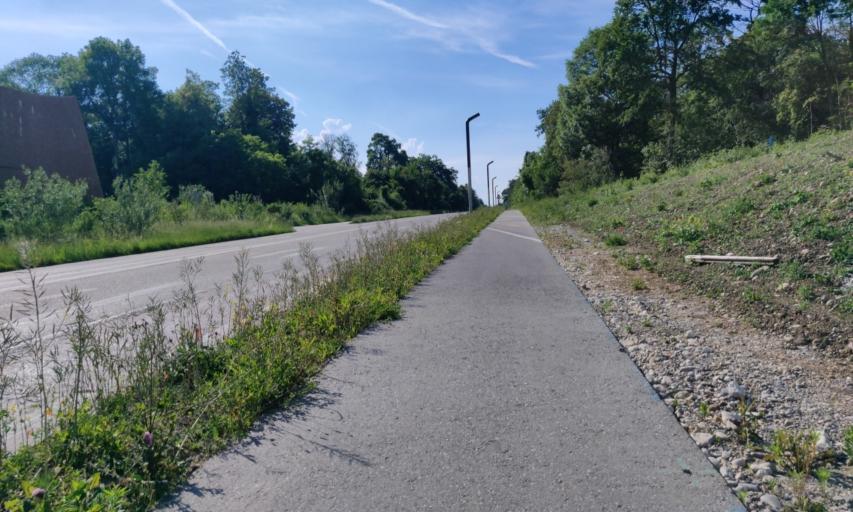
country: CH
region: Basel-Landschaft
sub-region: Bezirk Arlesheim
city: Muttenz
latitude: 47.5383
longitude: 7.6582
